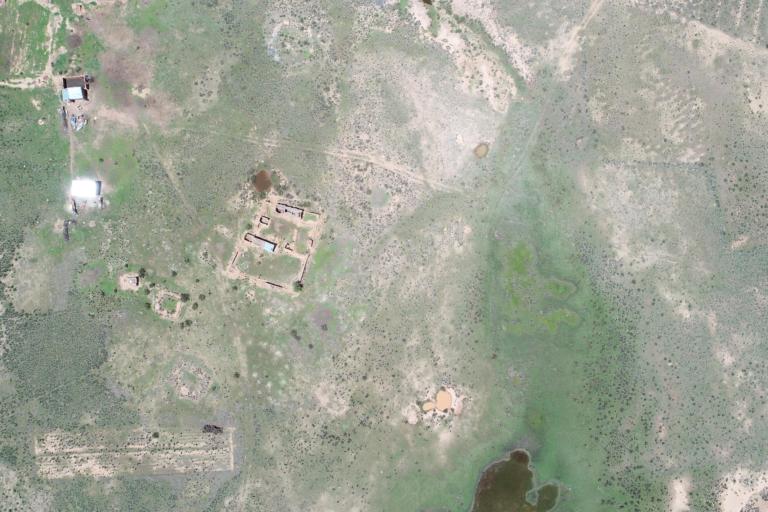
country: BO
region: La Paz
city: Curahuara de Carangas
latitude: -17.3125
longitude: -68.5180
